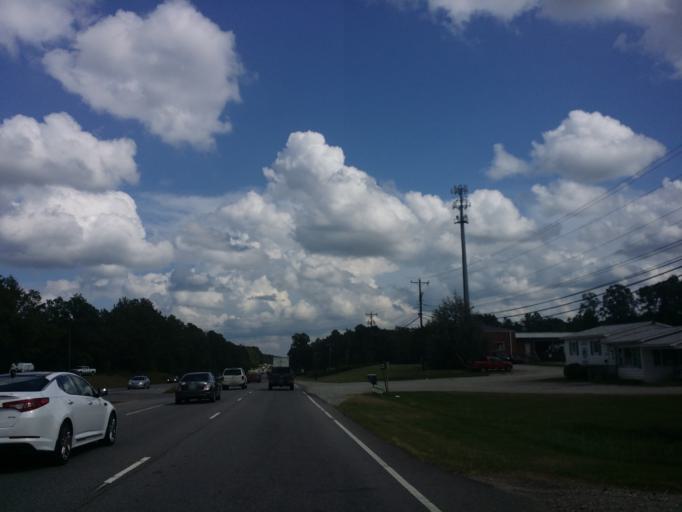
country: US
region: North Carolina
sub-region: Durham County
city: Durham
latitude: 35.9477
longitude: -78.8353
